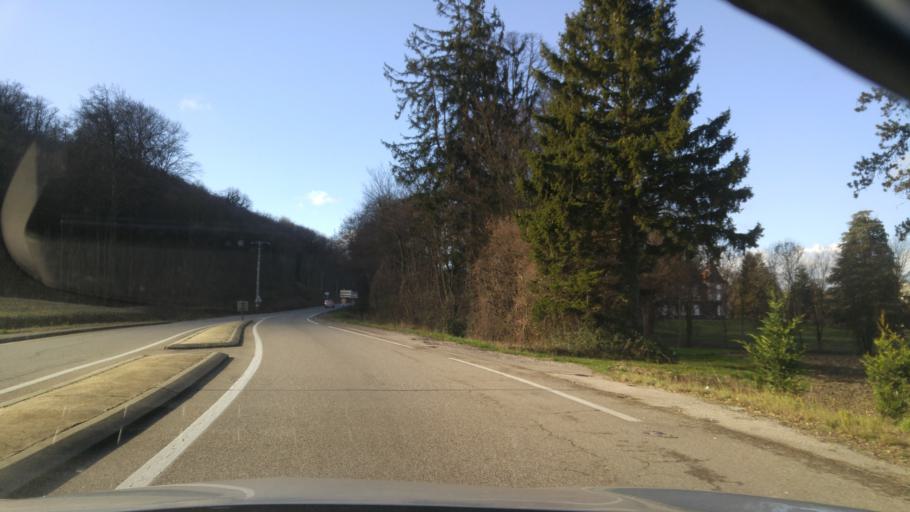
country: FR
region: Rhone-Alpes
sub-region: Departement de l'Isere
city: Villefontaine
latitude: 45.6035
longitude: 5.1591
